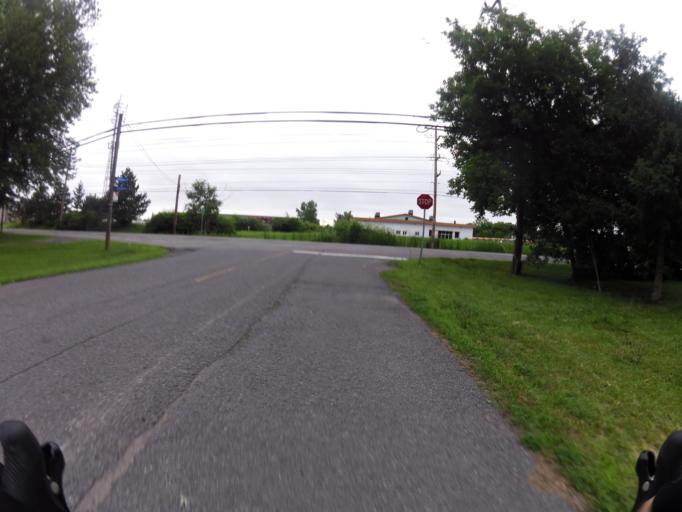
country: CA
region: Ontario
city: Ottawa
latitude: 45.3250
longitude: -75.7145
